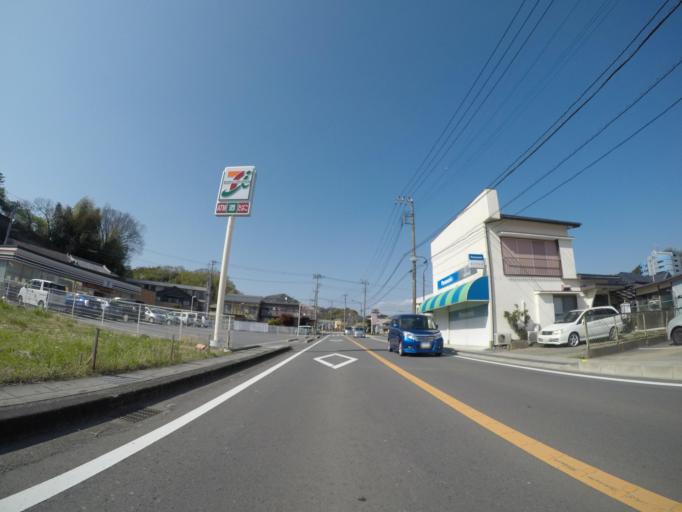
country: JP
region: Shizuoka
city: Mishima
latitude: 35.0321
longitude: 138.9290
